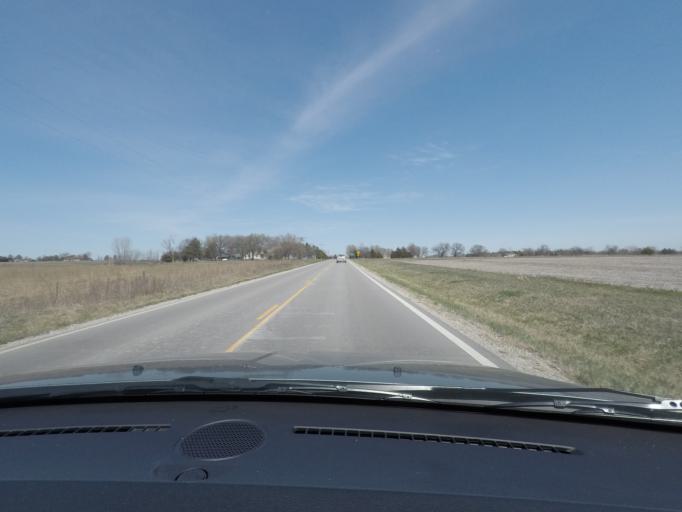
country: US
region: Kansas
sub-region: Lyon County
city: Emporia
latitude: 38.5020
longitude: -96.1707
